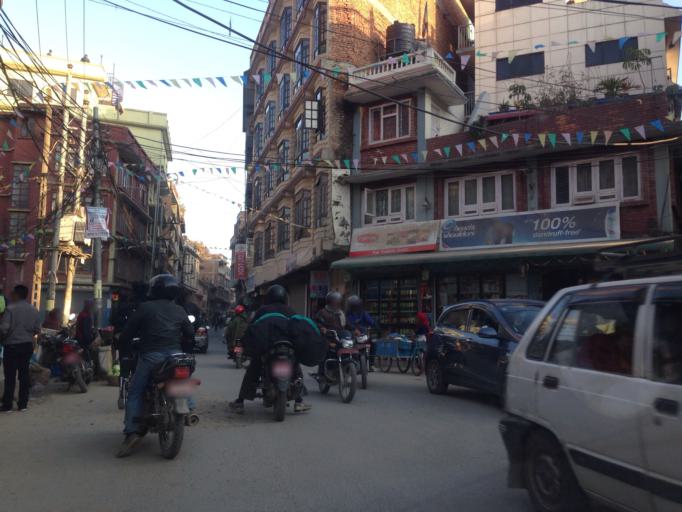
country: NP
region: Central Region
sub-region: Bagmati Zone
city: Kathmandu
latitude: 27.7130
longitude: 85.3040
